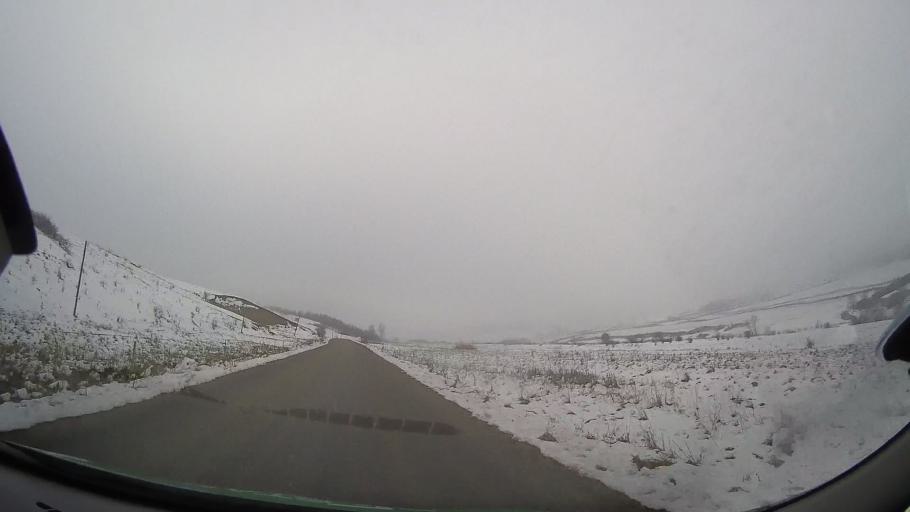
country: RO
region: Bacau
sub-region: Comuna Vultureni
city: Vultureni
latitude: 46.3163
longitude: 27.2929
